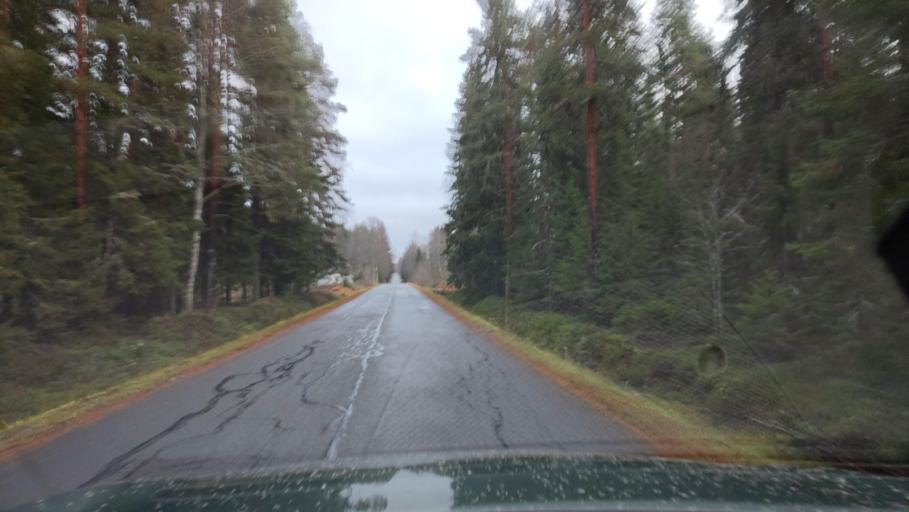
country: FI
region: Southern Ostrobothnia
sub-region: Suupohja
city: Teuva
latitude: 62.4577
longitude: 21.5854
